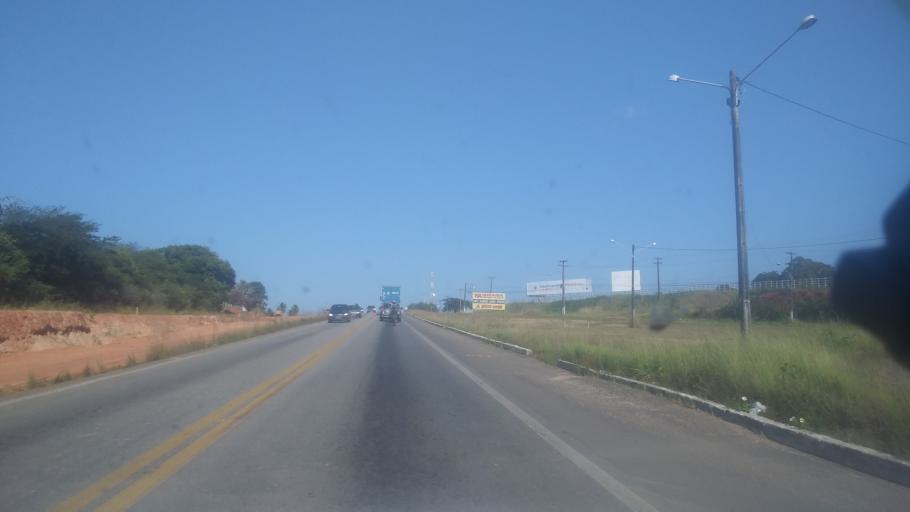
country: BR
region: Rio Grande do Norte
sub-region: Macaiba
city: Macaiba
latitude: -5.8671
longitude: -35.3660
